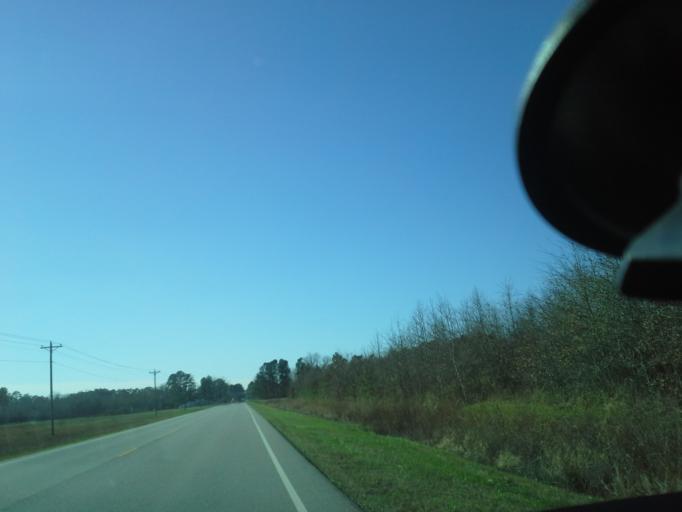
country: US
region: North Carolina
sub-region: Beaufort County
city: Belhaven
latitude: 35.5358
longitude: -76.7194
